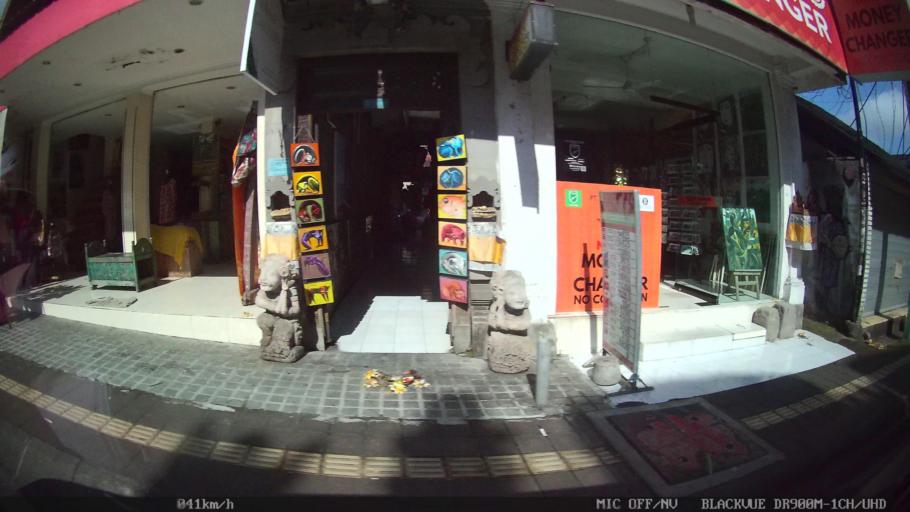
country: ID
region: Bali
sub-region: Kabupaten Gianyar
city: Ubud
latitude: -8.5142
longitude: 115.2609
